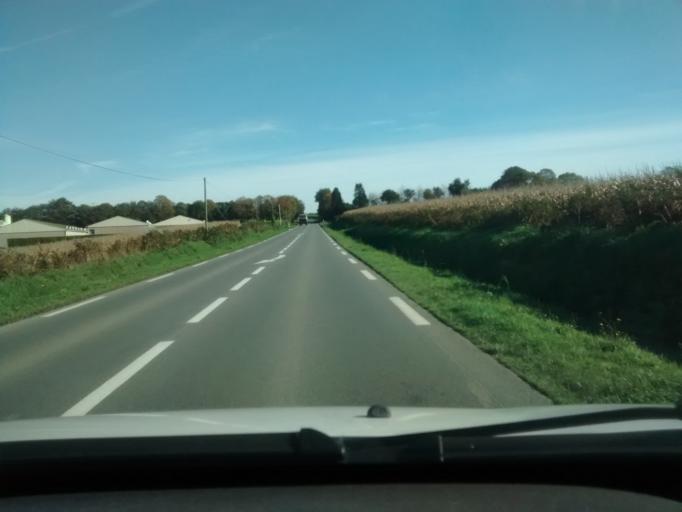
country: FR
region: Brittany
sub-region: Departement des Cotes-d'Armor
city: Langoat
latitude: 48.7632
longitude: -3.2875
